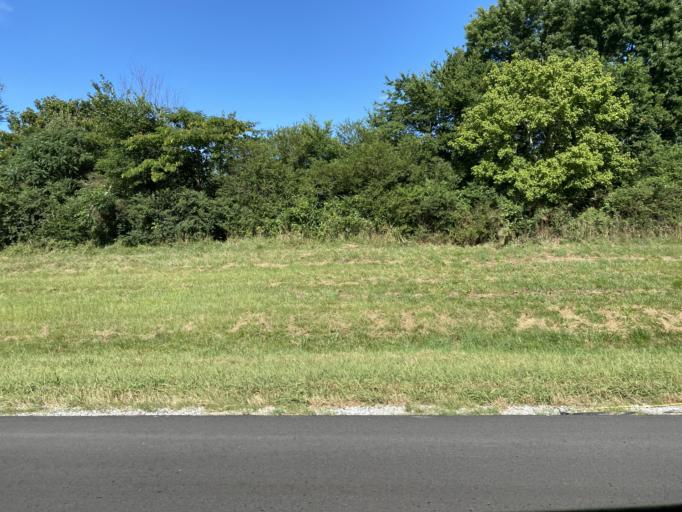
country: US
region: Alabama
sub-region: Limestone County
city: Athens
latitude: 34.7641
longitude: -86.9388
